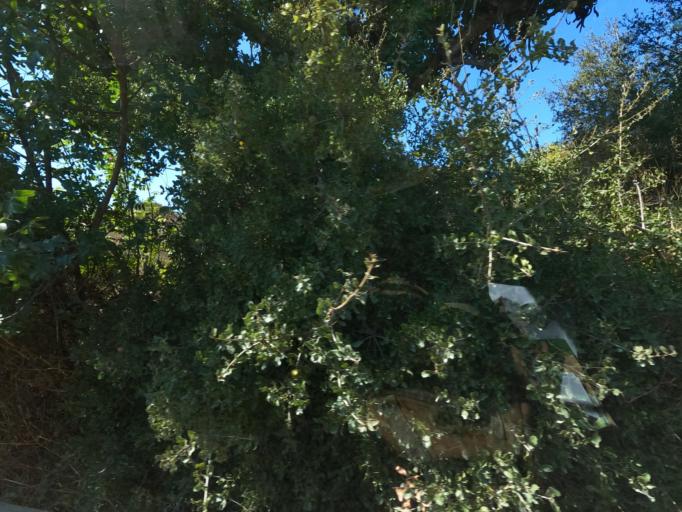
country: CY
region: Pafos
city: Polis
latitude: 34.9817
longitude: 32.4960
